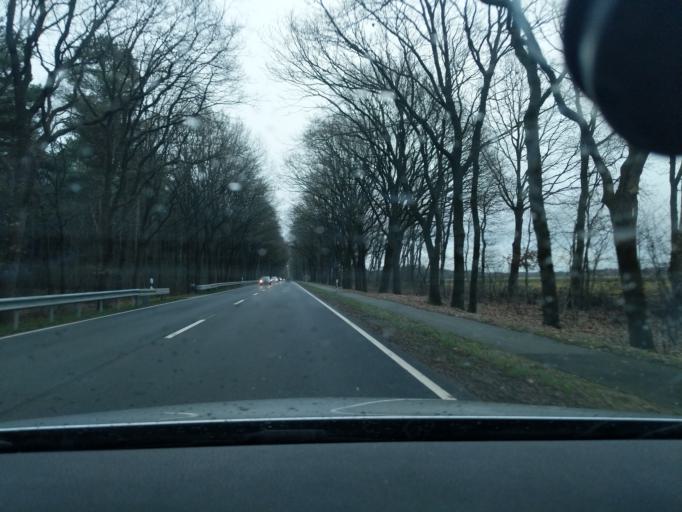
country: DE
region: Lower Saxony
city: Dudenbuttel
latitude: 53.5586
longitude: 9.3649
